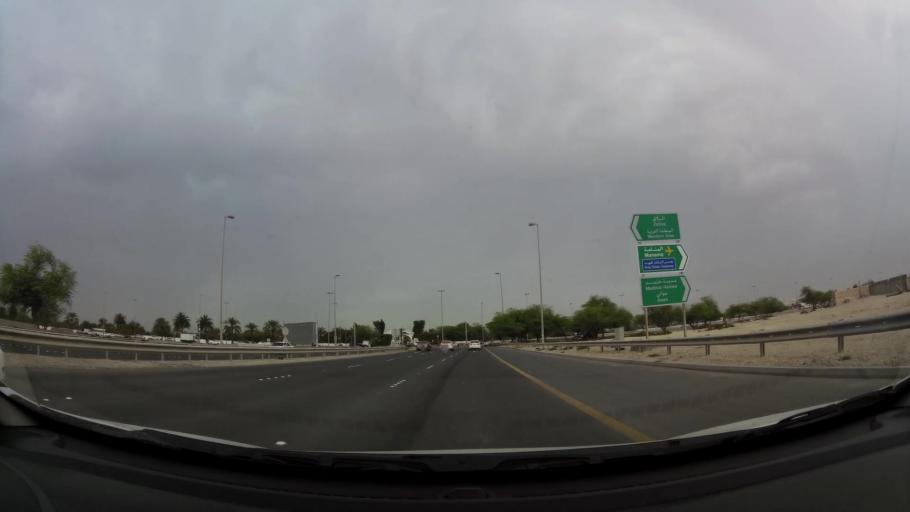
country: BH
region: Central Governorate
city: Dar Kulayb
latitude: 26.0557
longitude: 50.4999
